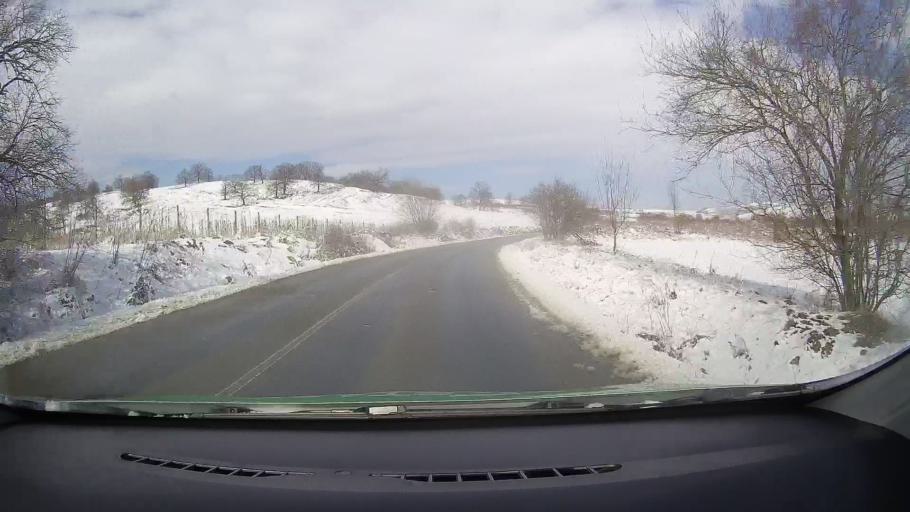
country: RO
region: Sibiu
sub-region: Comuna Altina
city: Altina
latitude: 45.9471
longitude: 24.4506
